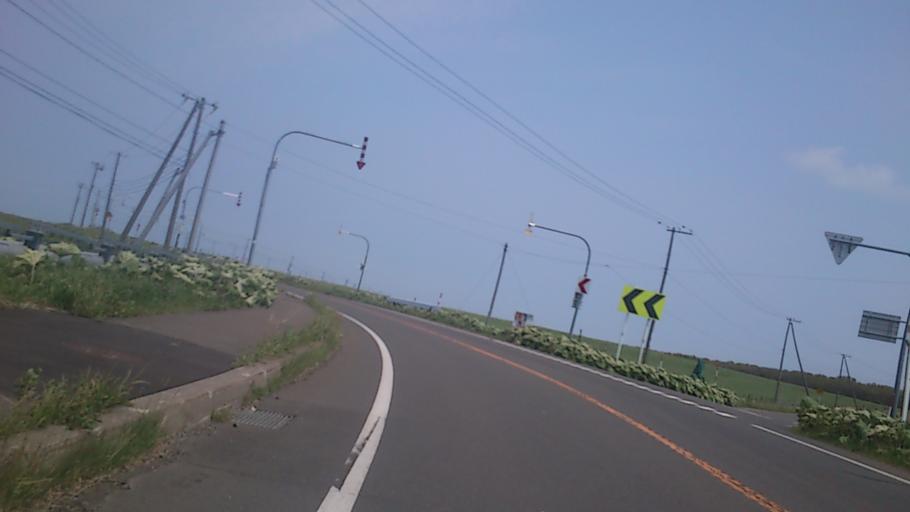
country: JP
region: Hokkaido
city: Nemuro
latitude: 43.3557
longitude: 145.6122
